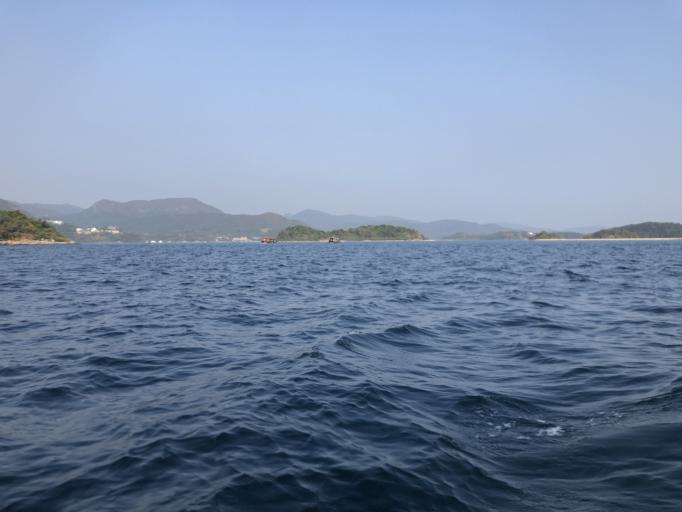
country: HK
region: Sai Kung
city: Sai Kung
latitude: 22.3761
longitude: 114.2799
